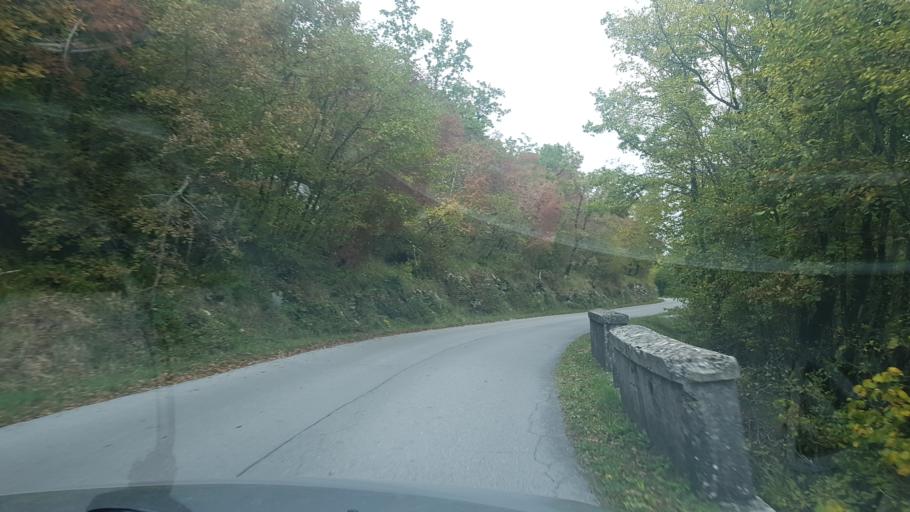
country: SI
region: Hrpelje-Kozina
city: Kozina
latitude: 45.5121
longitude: 13.9637
